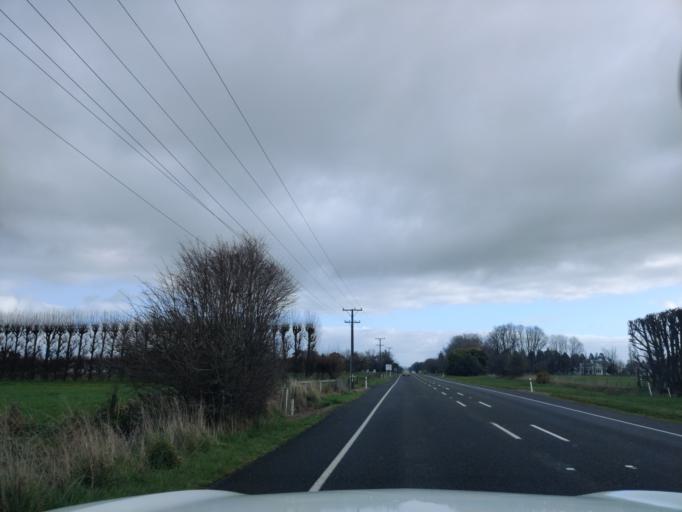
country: NZ
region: Manawatu-Wanganui
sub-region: Palmerston North City
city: Palmerston North
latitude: -40.3298
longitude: 175.5870
